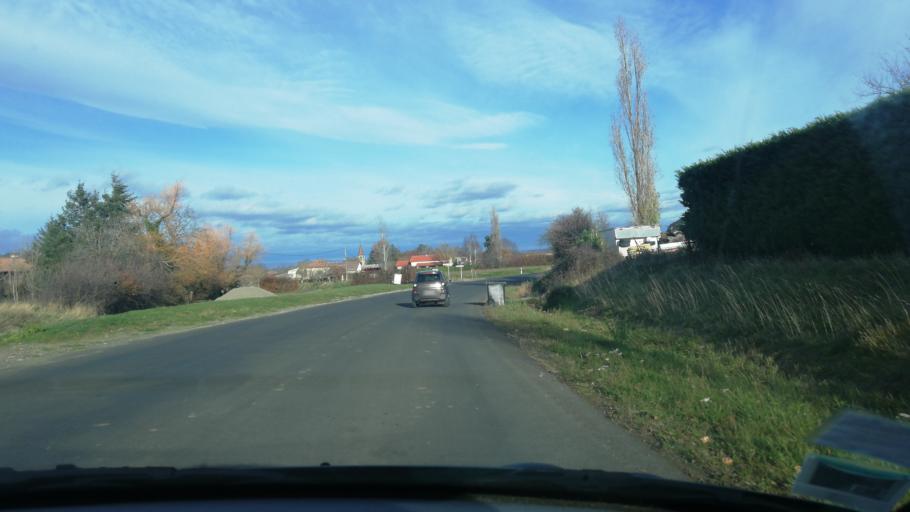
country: FR
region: Auvergne
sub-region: Departement du Puy-de-Dome
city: Billom
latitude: 45.7135
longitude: 3.3475
